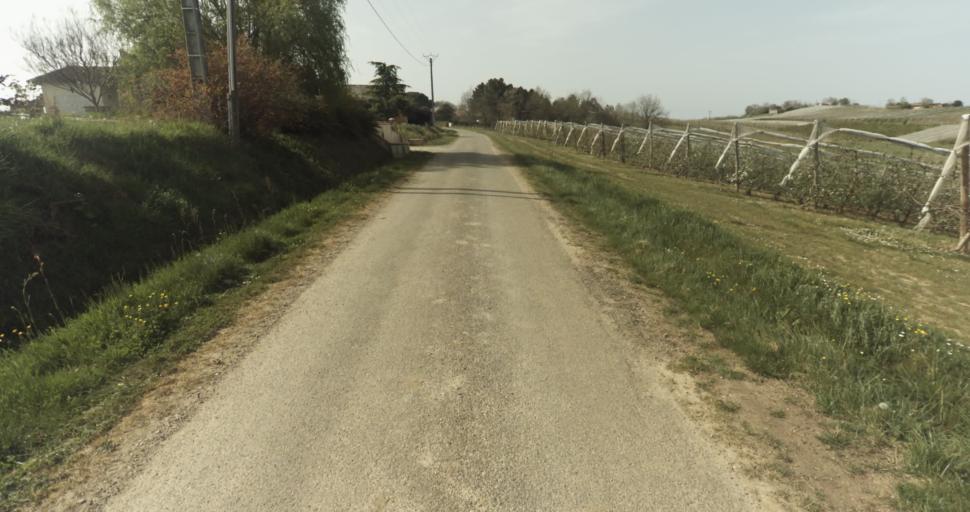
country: FR
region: Midi-Pyrenees
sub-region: Departement du Tarn-et-Garonne
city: Lafrancaise
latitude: 44.1462
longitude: 1.1672
